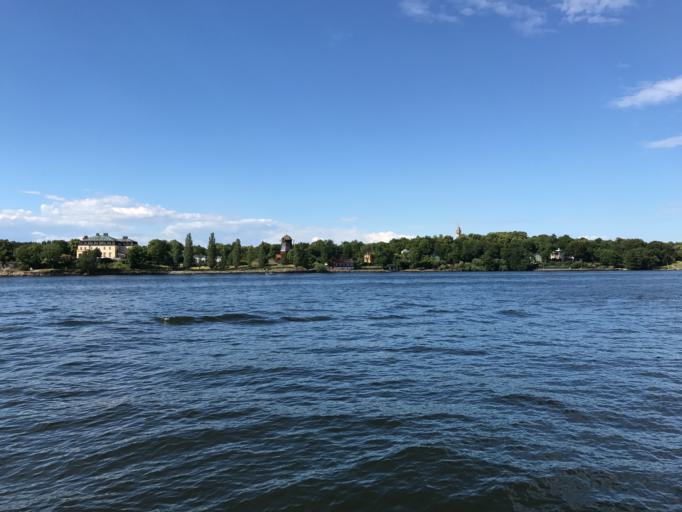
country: SE
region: Stockholm
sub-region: Stockholms Kommun
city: OEstermalm
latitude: 59.3160
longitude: 18.1164
